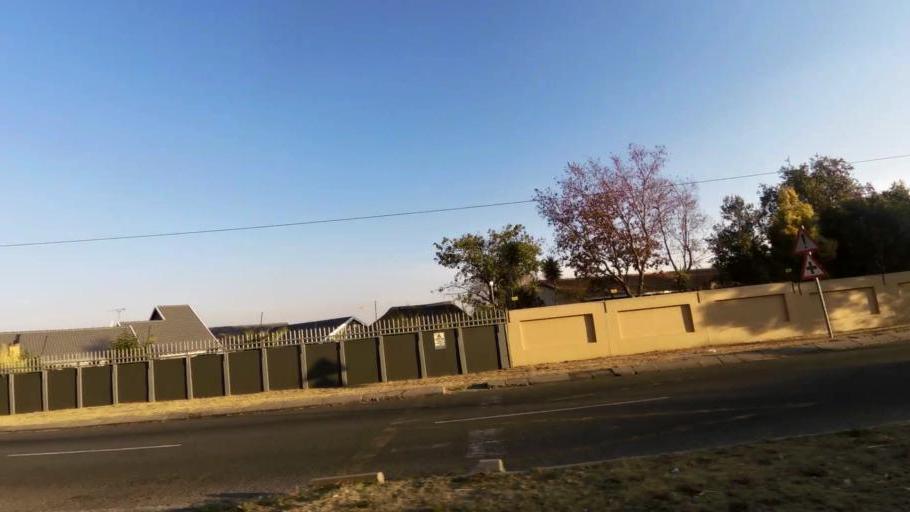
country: ZA
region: Gauteng
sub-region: City of Johannesburg Metropolitan Municipality
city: Roodepoort
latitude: -26.1639
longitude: 27.9535
